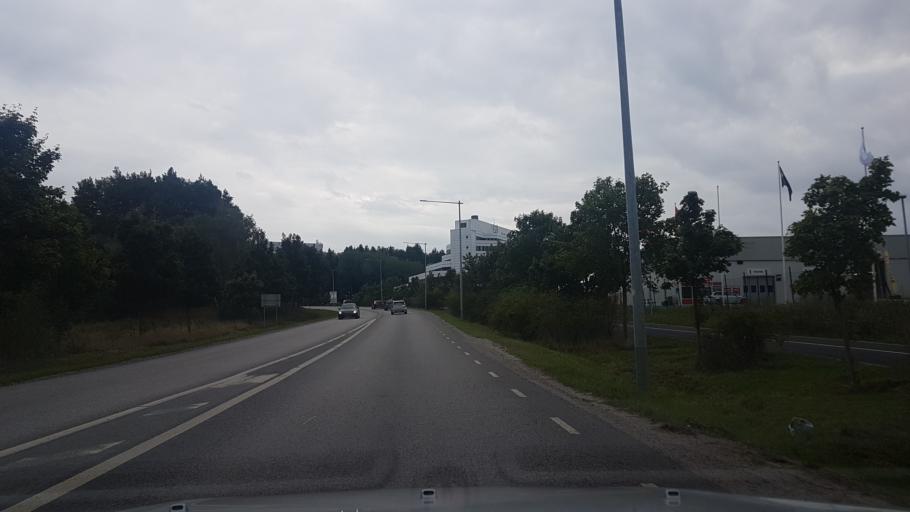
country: SE
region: Stockholm
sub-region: Jarfalla Kommun
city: Jakobsberg
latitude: 59.4136
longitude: 17.8285
